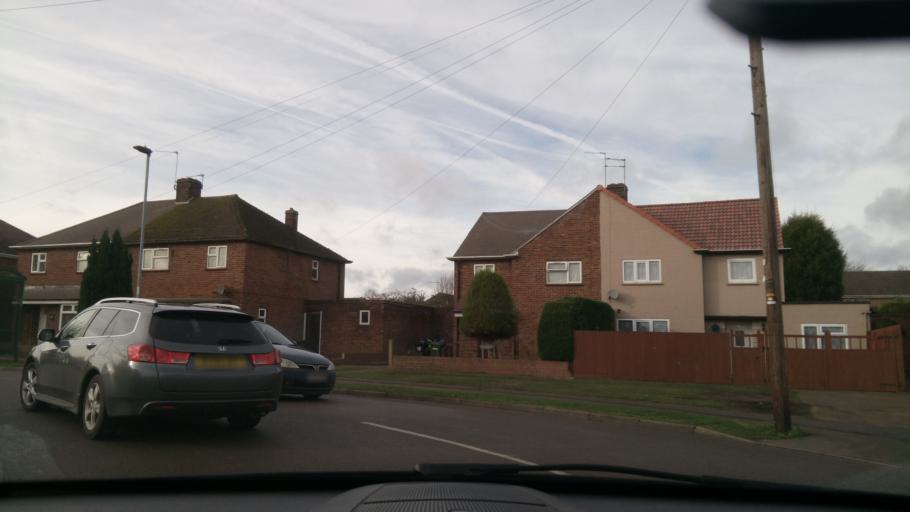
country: GB
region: England
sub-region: Peterborough
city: Peterborough
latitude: 52.5843
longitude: -0.2238
